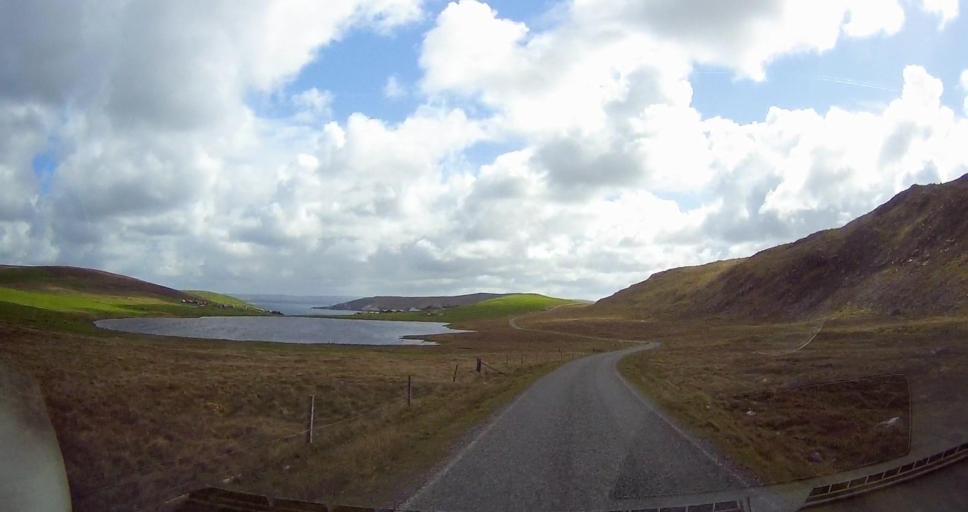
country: GB
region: Scotland
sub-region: Shetland Islands
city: Lerwick
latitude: 60.5531
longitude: -1.3394
